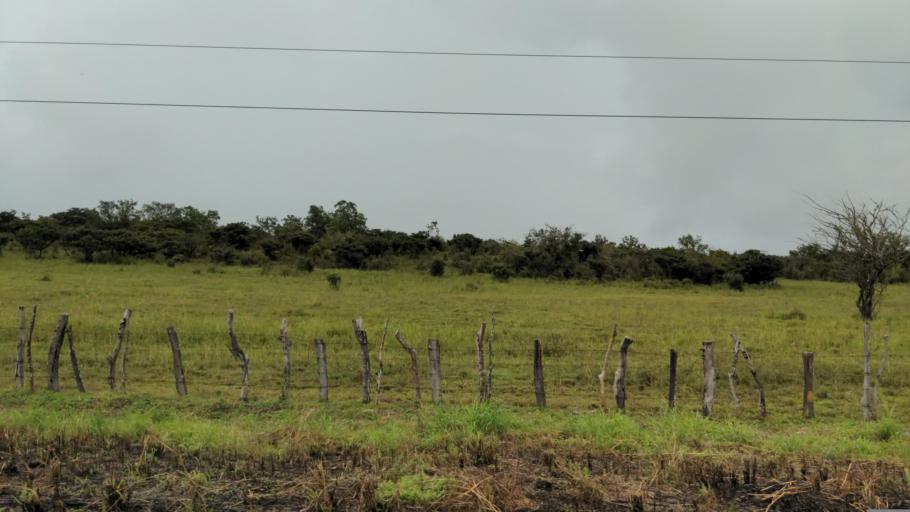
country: CR
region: Guanacaste
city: Liberia
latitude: 10.5984
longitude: -85.5230
